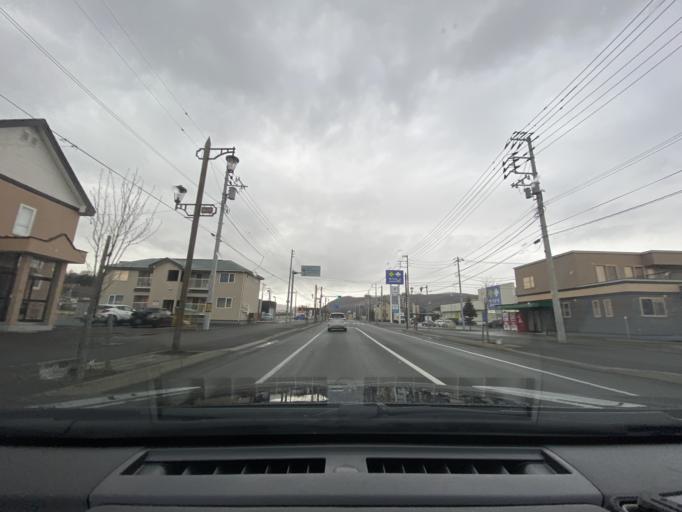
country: JP
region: Hokkaido
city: Otofuke
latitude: 43.2459
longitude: 143.5471
